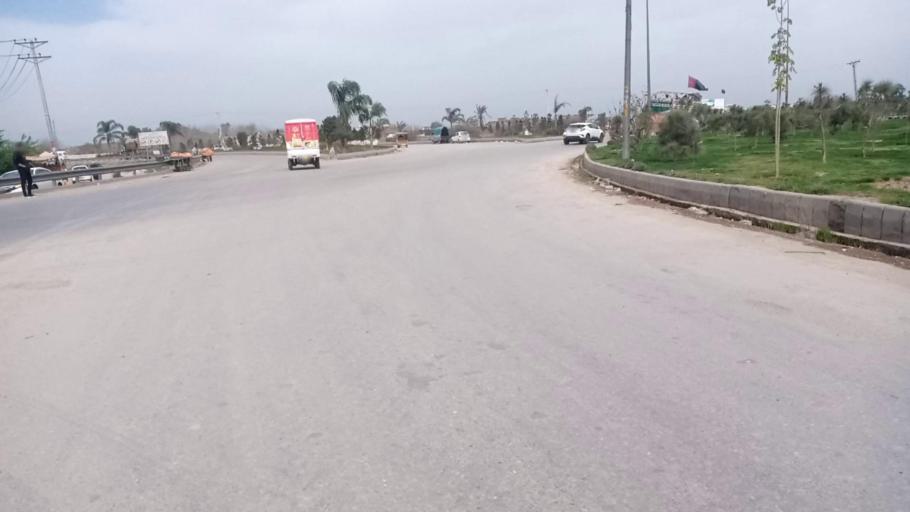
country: PK
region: Khyber Pakhtunkhwa
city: Peshawar
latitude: 34.0265
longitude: 71.6439
